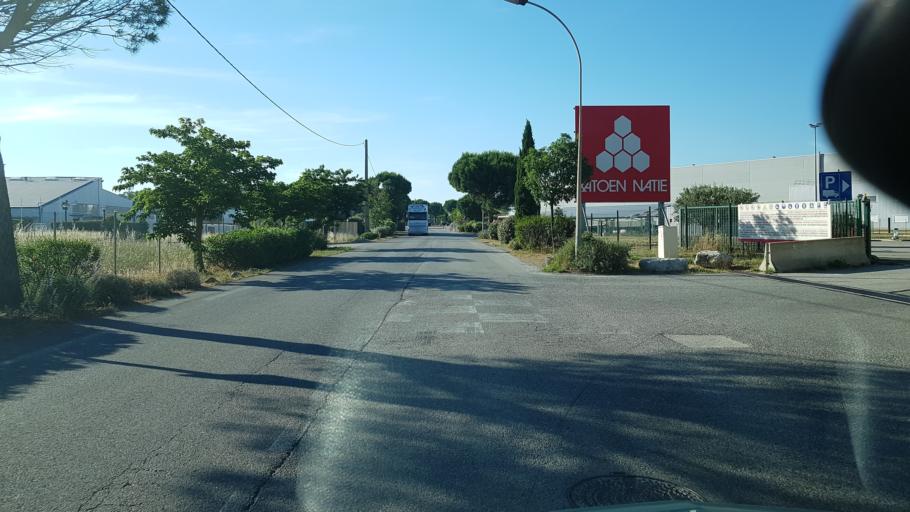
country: FR
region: Provence-Alpes-Cote d'Azur
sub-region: Departement des Bouches-du-Rhone
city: Saint-Martin-de-Crau
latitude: 43.6190
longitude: 4.7937
